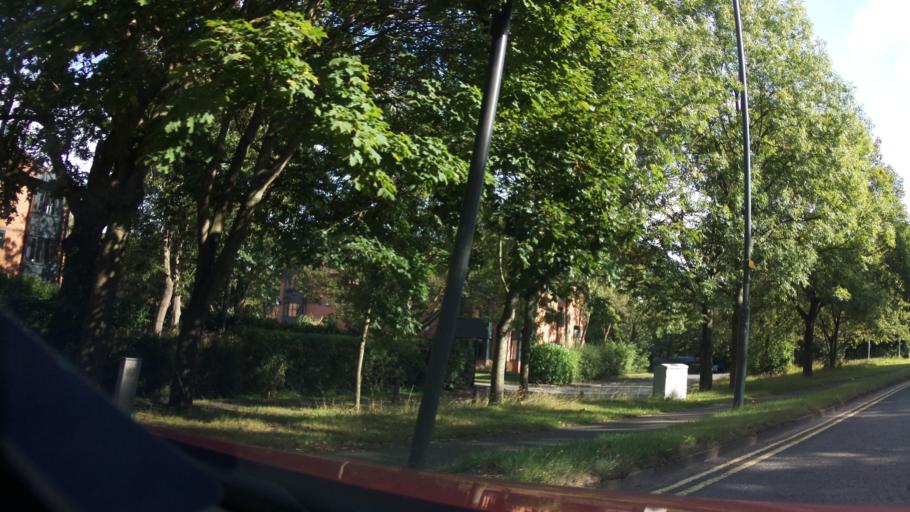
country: GB
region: England
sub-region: Derby
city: Derby
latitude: 52.9361
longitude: -1.4996
